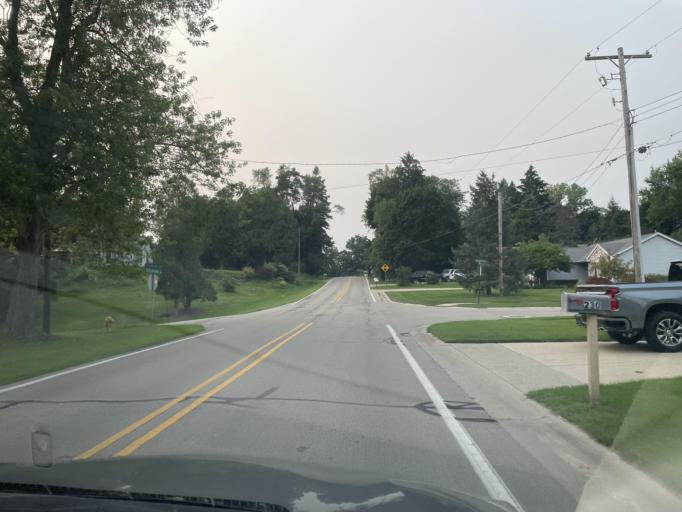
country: US
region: Michigan
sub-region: Kent County
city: Walker
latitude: 42.9687
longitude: -85.7371
